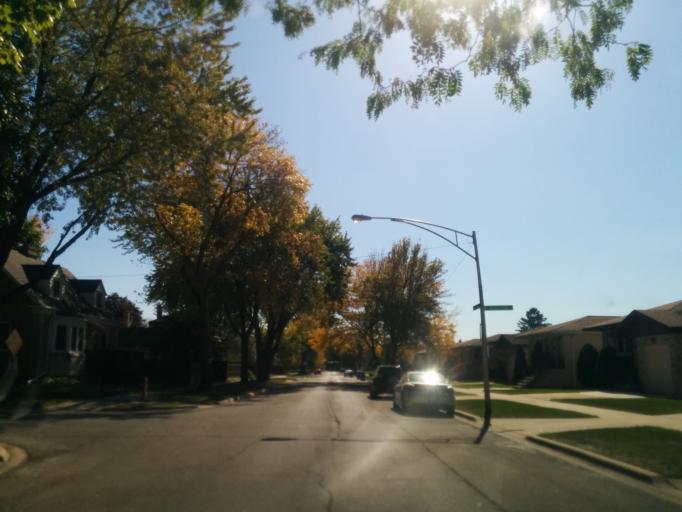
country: US
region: Illinois
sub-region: Cook County
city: Elmwood Park
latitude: 41.9429
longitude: -87.7921
